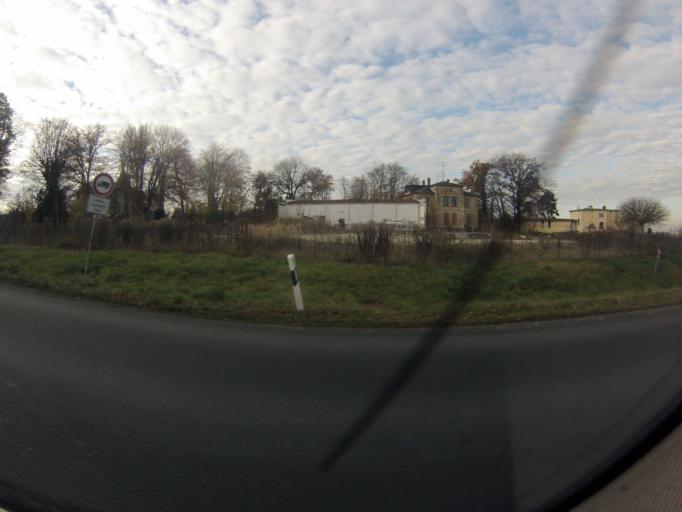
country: DE
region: Saxony
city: Meerane
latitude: 50.8524
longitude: 12.4467
